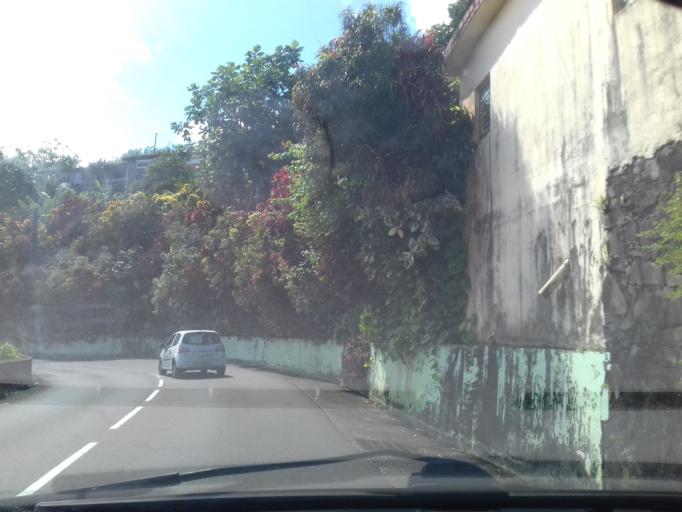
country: MQ
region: Martinique
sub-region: Martinique
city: Saint-Joseph
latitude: 14.6697
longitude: -61.0492
